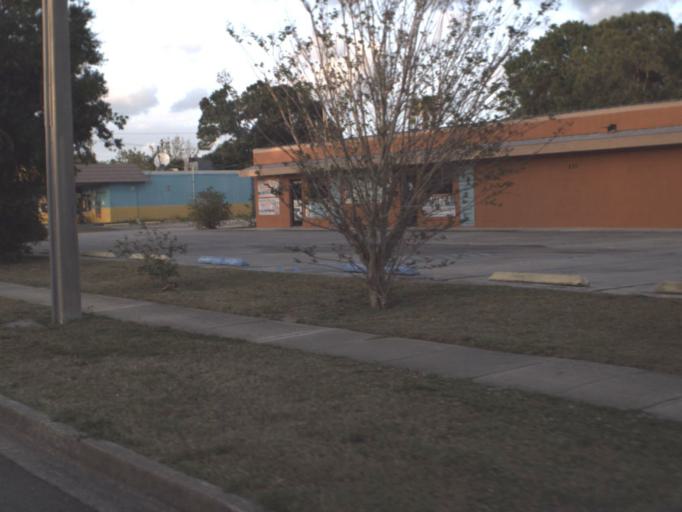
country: US
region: Florida
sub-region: Brevard County
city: Rockledge
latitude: 28.3480
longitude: -80.7424
